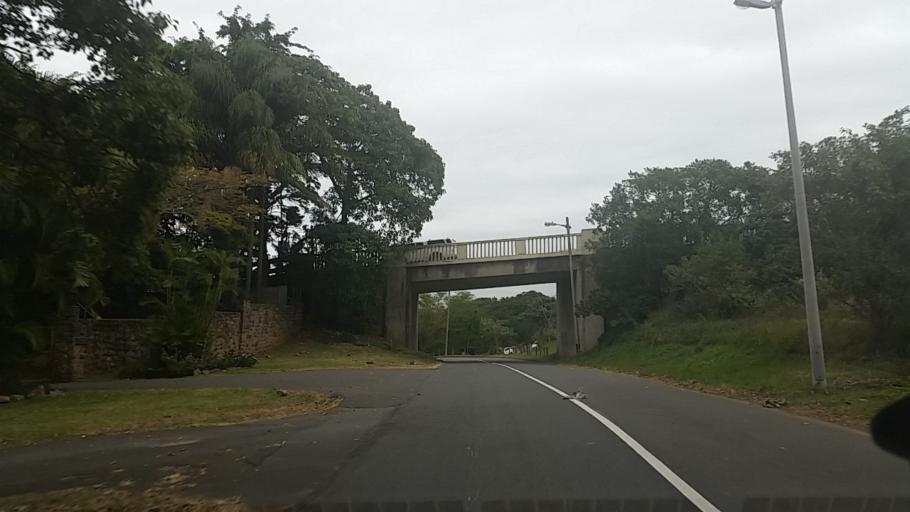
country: ZA
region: KwaZulu-Natal
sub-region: eThekwini Metropolitan Municipality
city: Berea
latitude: -29.8330
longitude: 30.9231
